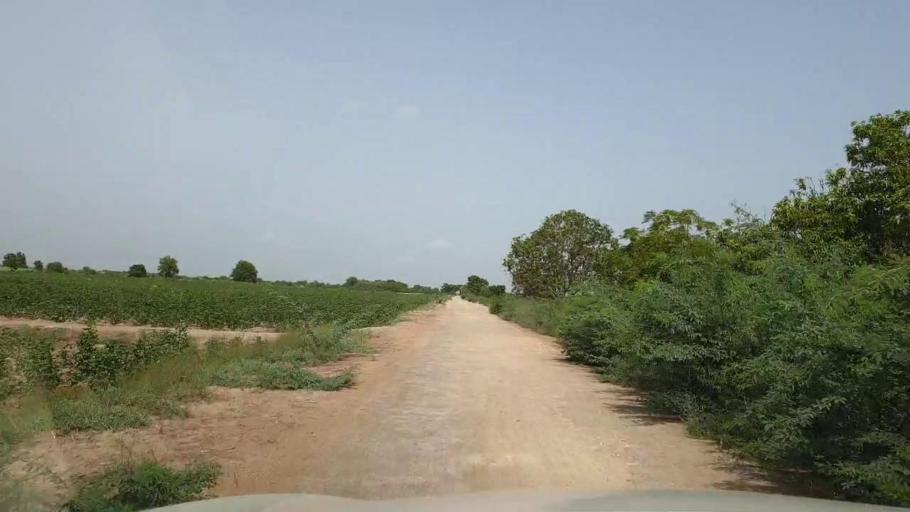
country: PK
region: Sindh
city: Mirwah Gorchani
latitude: 25.2561
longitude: 68.9409
